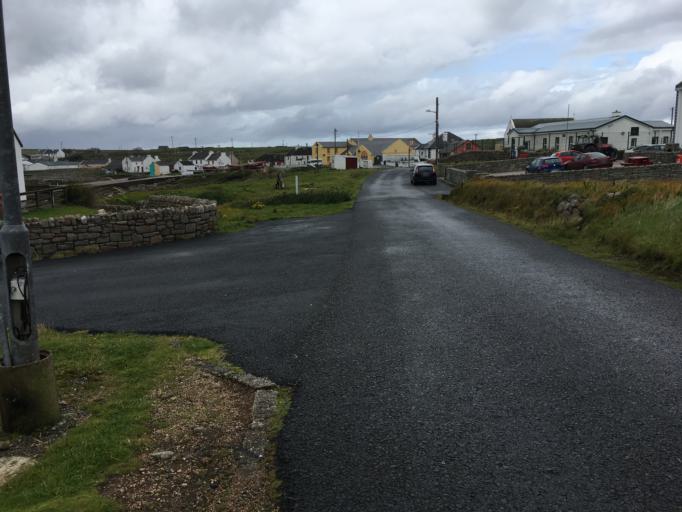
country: IE
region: Ulster
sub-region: County Donegal
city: Derrybeg
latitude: 55.2644
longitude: -8.2237
